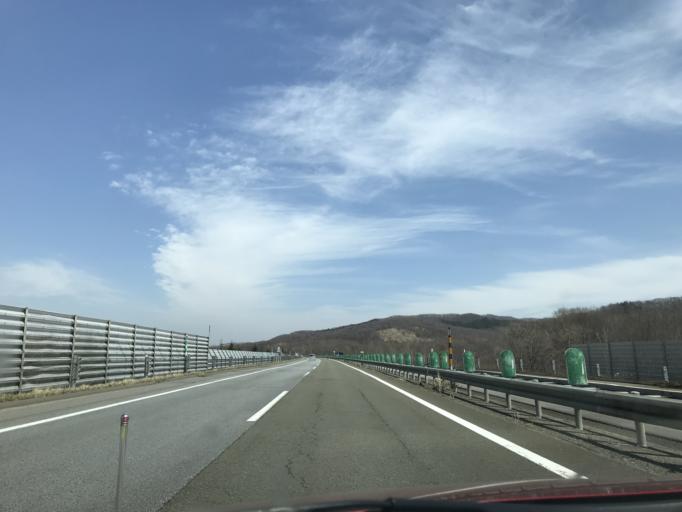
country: JP
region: Hokkaido
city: Bibai
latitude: 43.2661
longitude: 141.8422
